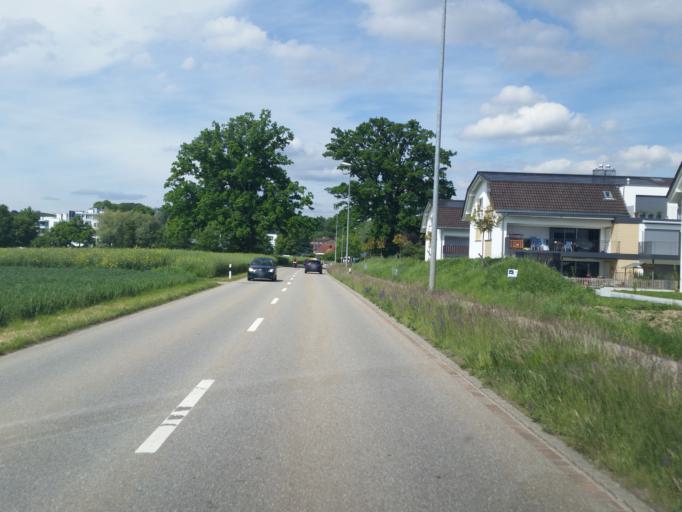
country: CH
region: Aargau
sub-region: Bezirk Muri
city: Waltenschwil
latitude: 47.3333
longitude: 8.2970
